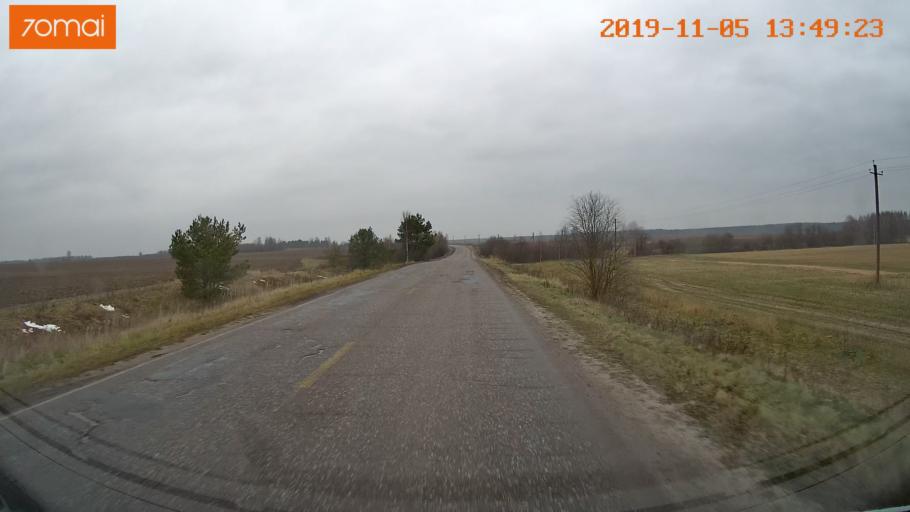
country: RU
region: Ivanovo
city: Kaminskiy
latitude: 57.0101
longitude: 41.4094
